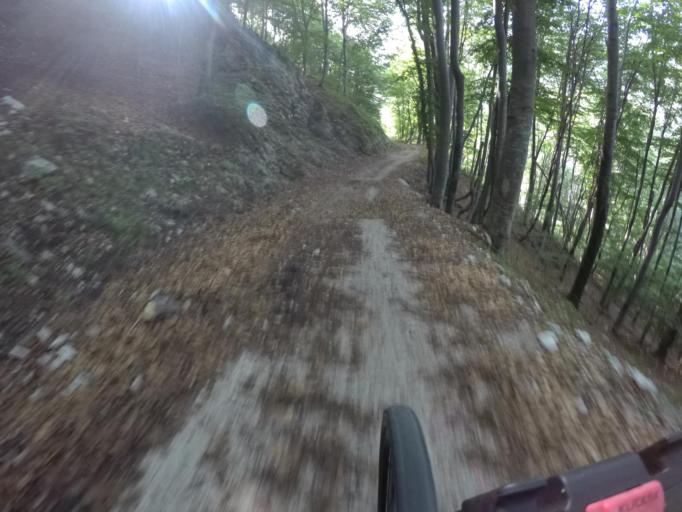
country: IT
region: Friuli Venezia Giulia
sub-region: Provincia di Udine
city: Resiutta
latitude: 46.3263
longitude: 13.2182
